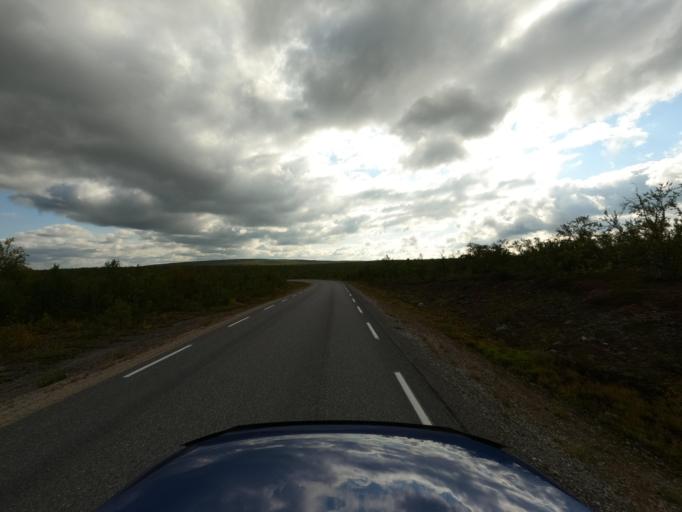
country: NO
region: Finnmark Fylke
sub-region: Porsanger
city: Lakselv
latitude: 69.3690
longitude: 24.2839
